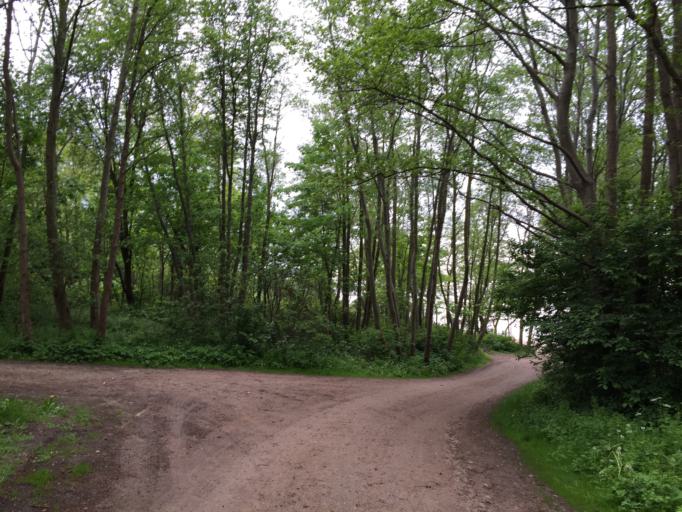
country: LT
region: Klaipedos apskritis
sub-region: Klaipeda
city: Klaipeda
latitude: 55.8070
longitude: 21.0675
